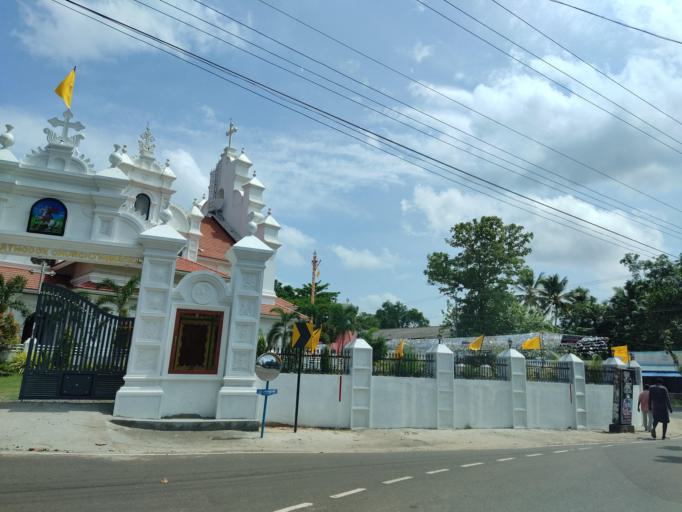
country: IN
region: Kerala
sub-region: Alappuzha
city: Mavelikara
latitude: 9.2773
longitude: 76.5676
